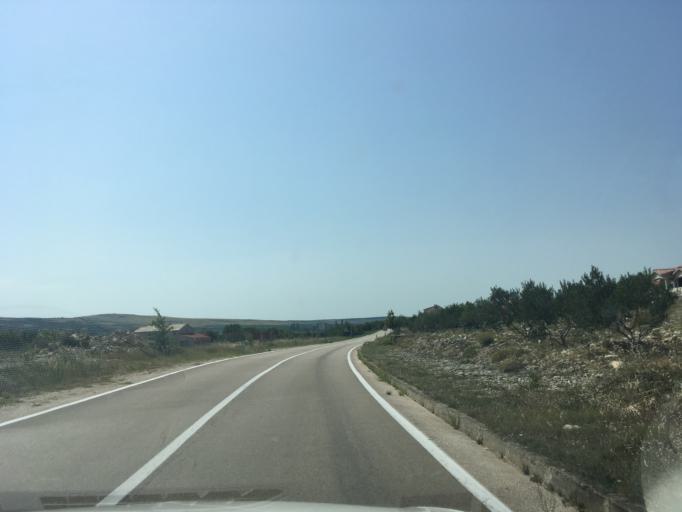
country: HR
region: Zadarska
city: Benkovac
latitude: 43.9653
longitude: 15.7297
